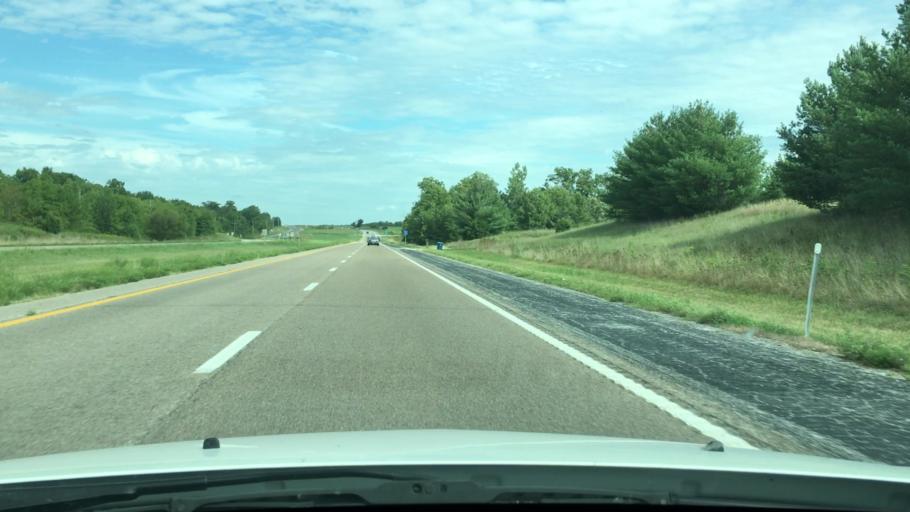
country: US
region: Missouri
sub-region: Audrain County
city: Mexico
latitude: 39.0560
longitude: -91.8943
